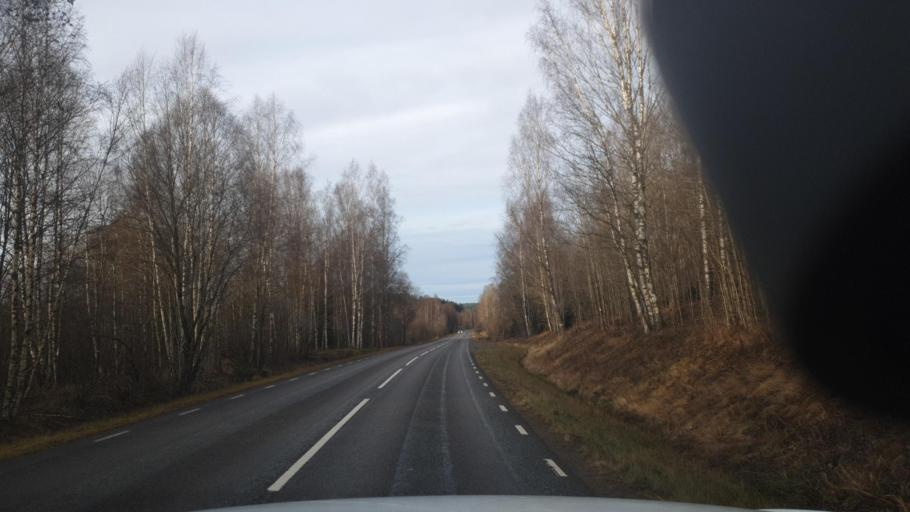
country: SE
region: Vaermland
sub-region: Eda Kommun
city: Amotfors
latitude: 59.6863
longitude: 12.0988
